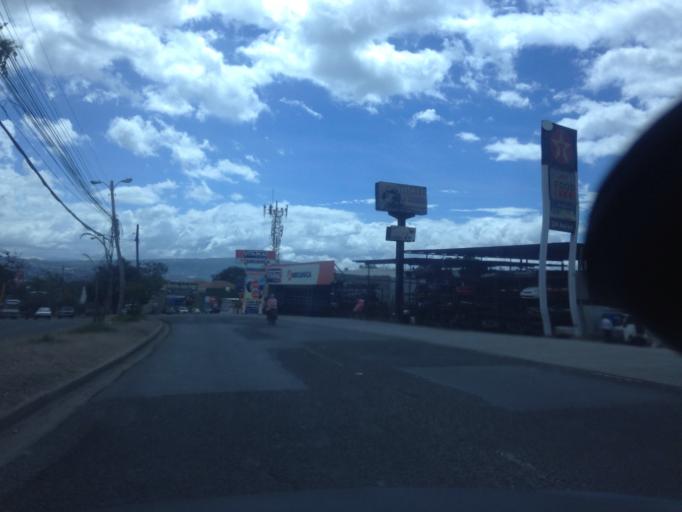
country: HN
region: Francisco Morazan
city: Tegucigalpa
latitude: 14.0750
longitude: -87.1813
